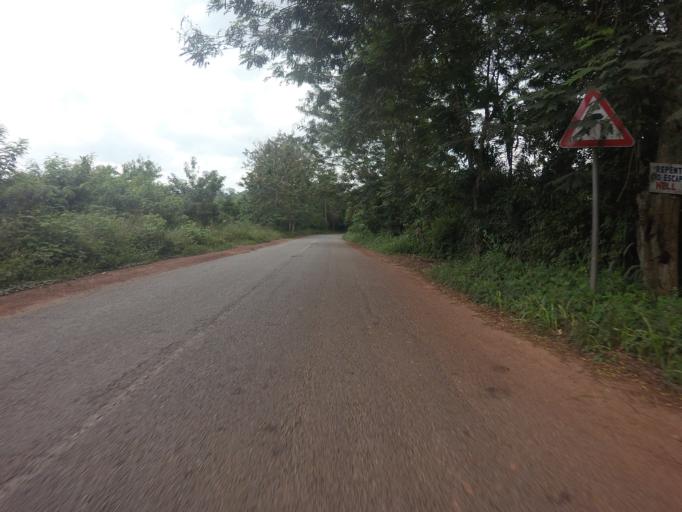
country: GH
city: Akropong
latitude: 5.9585
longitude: -0.1264
